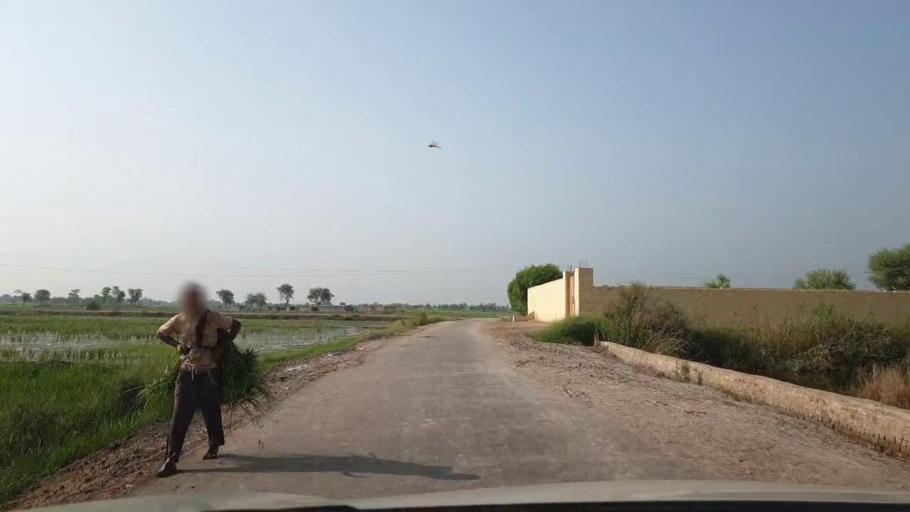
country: PK
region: Sindh
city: Larkana
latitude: 27.4912
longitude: 68.2117
